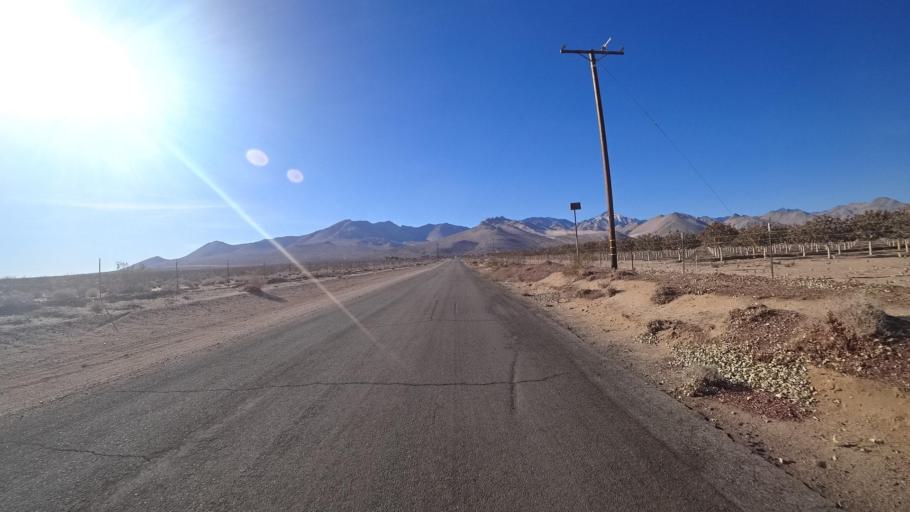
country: US
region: California
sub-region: Kern County
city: Inyokern
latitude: 35.6813
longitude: -117.8366
